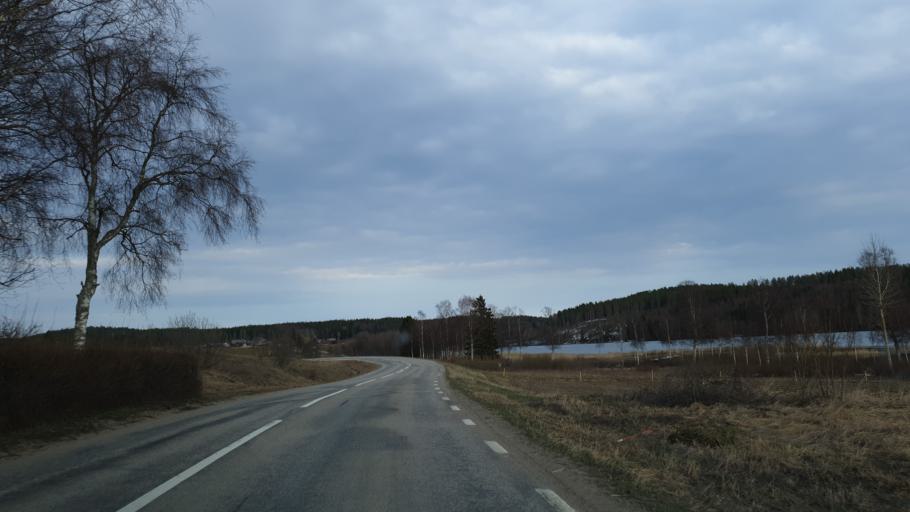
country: SE
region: Gaevleborg
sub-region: Nordanstigs Kommun
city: Bergsjoe
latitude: 61.9791
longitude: 17.2684
